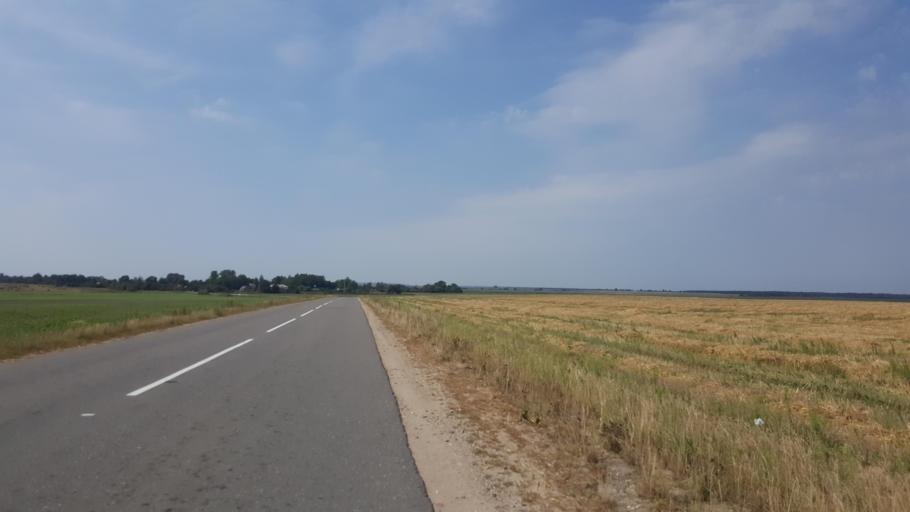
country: BY
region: Brest
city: Kamyanyets
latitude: 52.4737
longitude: 23.7060
